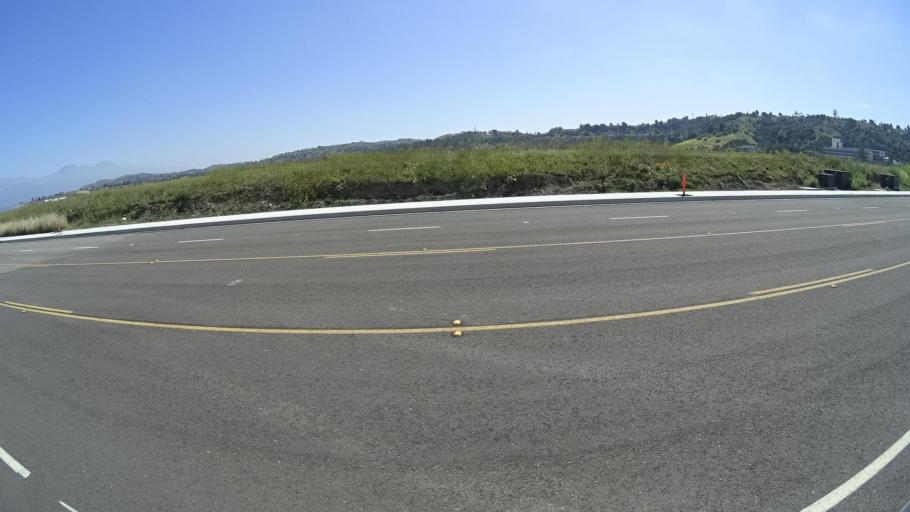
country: US
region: California
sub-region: Los Angeles County
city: Diamond Bar
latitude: 34.0065
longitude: -117.8341
